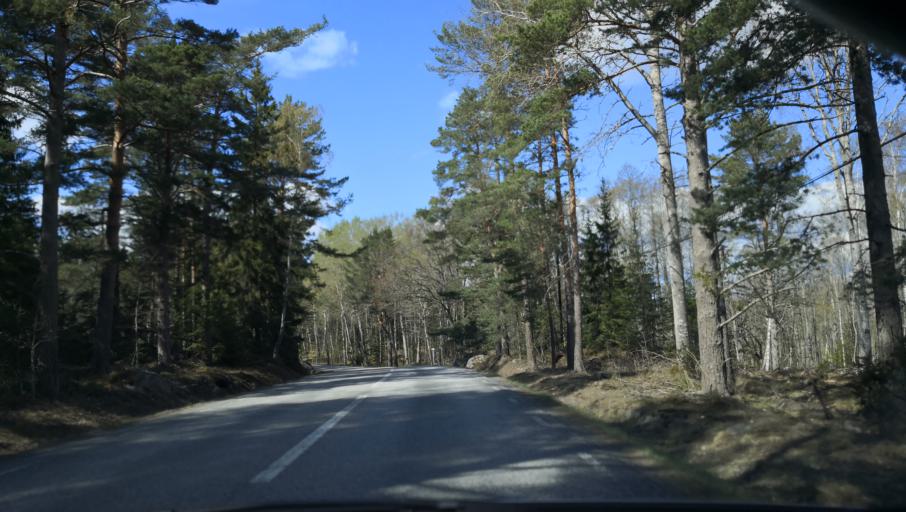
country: SE
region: Stockholm
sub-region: Varmdo Kommun
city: Hemmesta
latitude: 59.3809
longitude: 18.5229
